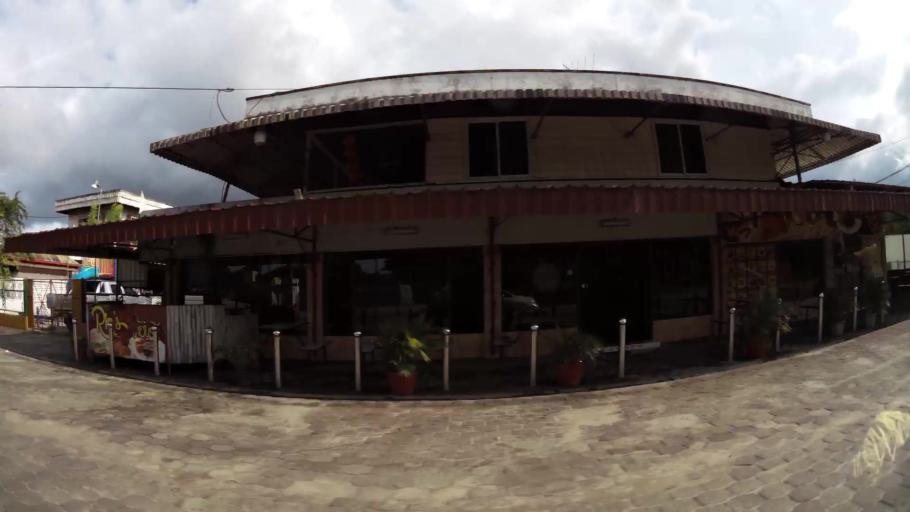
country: SR
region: Paramaribo
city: Paramaribo
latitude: 5.8429
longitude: -55.2109
